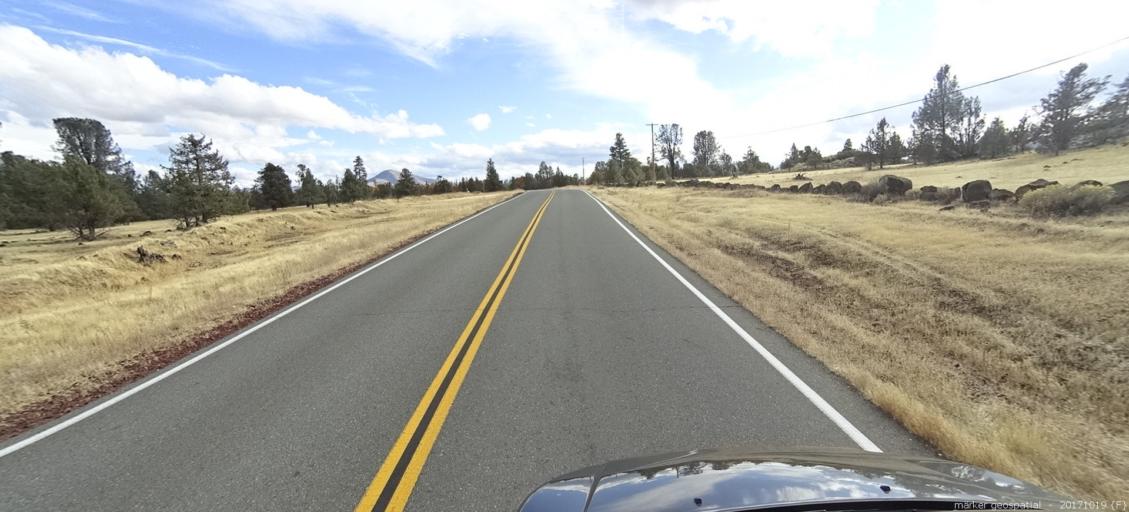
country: US
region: California
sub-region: Shasta County
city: Burney
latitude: 40.9929
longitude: -121.4301
